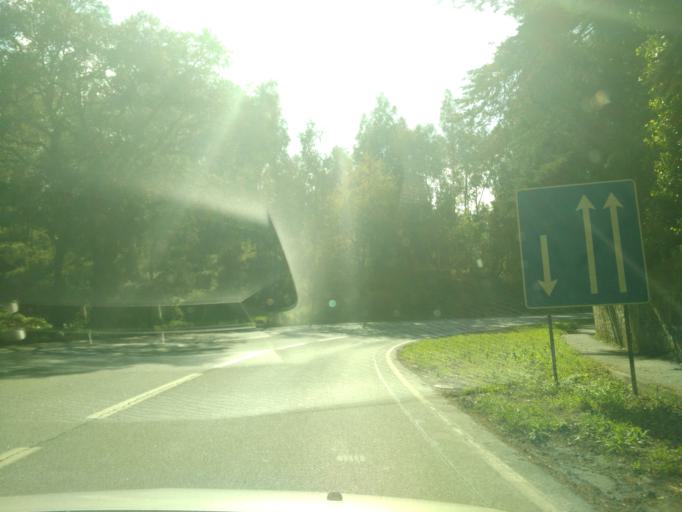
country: PT
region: Braga
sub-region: Braga
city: Braga
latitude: 41.5378
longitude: -8.4199
